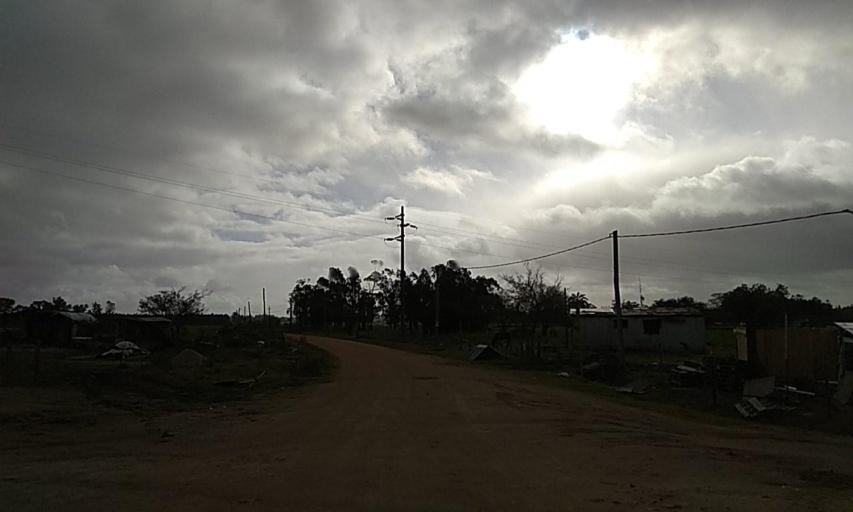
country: UY
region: Florida
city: Florida
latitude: -34.0744
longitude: -56.2336
